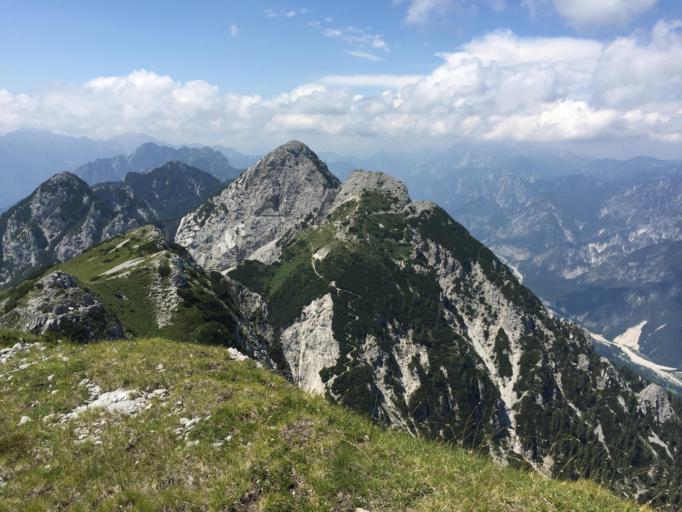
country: IT
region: Friuli Venezia Giulia
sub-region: Provincia di Udine
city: Malborghetto
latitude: 46.4747
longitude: 13.4331
